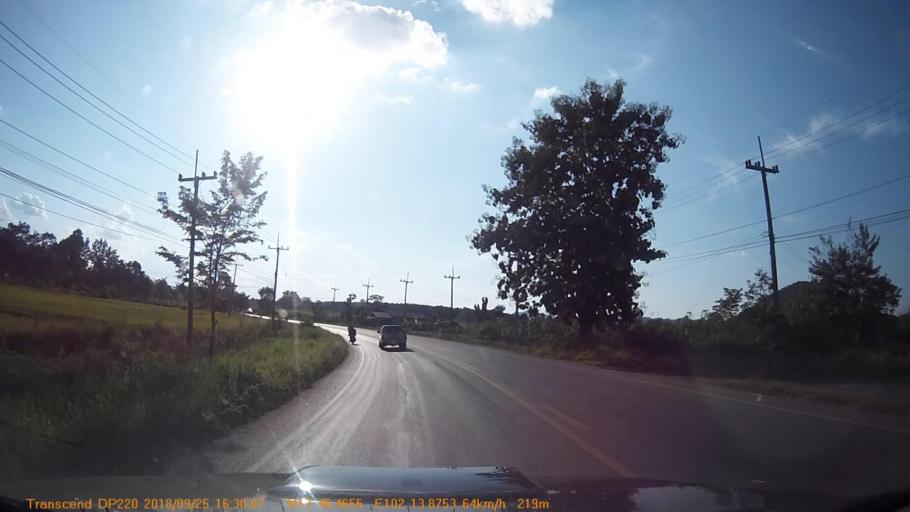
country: TH
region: Changwat Udon Thani
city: Nam Som
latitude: 17.7744
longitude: 102.2312
